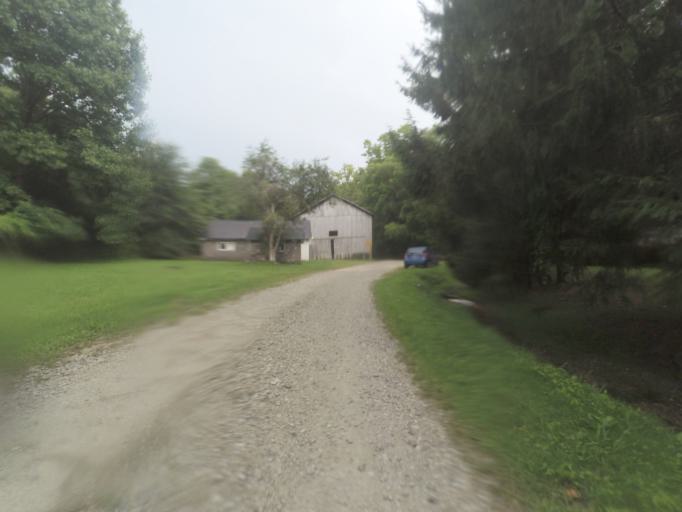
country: US
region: West Virginia
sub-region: Cabell County
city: Huntington
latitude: 38.3789
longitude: -82.3946
